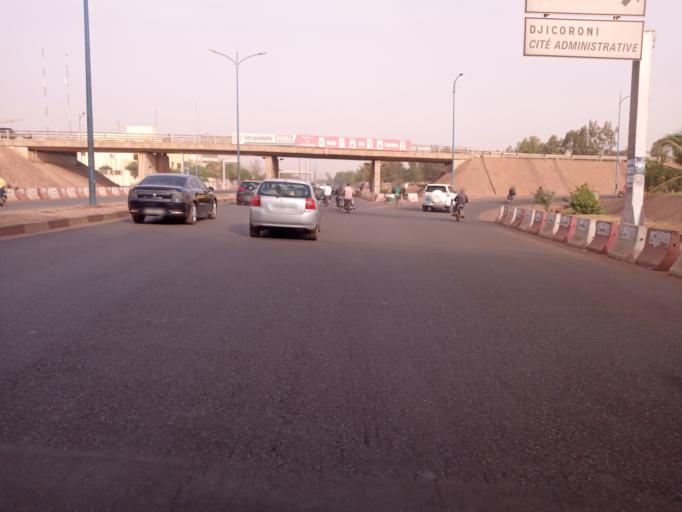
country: ML
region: Bamako
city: Bamako
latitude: 12.6320
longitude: -8.0113
